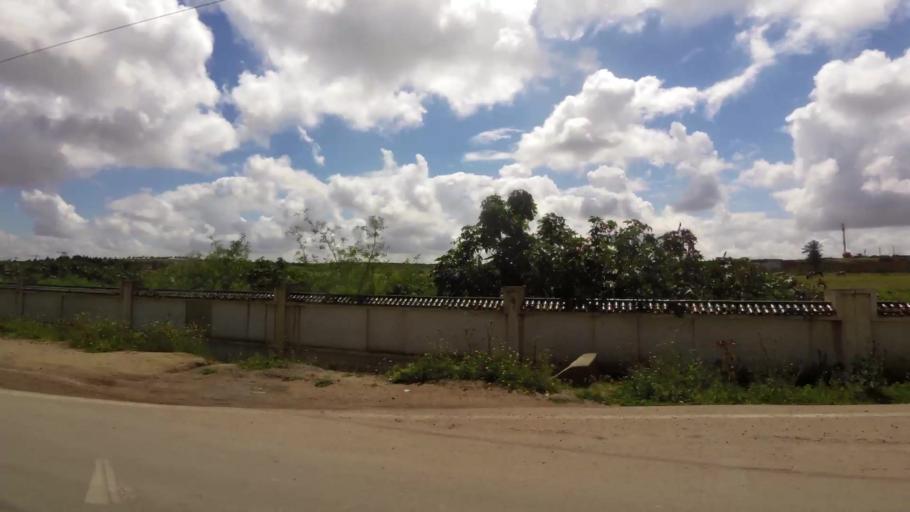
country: MA
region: Grand Casablanca
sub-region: Nouaceur
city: Dar Bouazza
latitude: 33.5282
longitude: -7.7342
